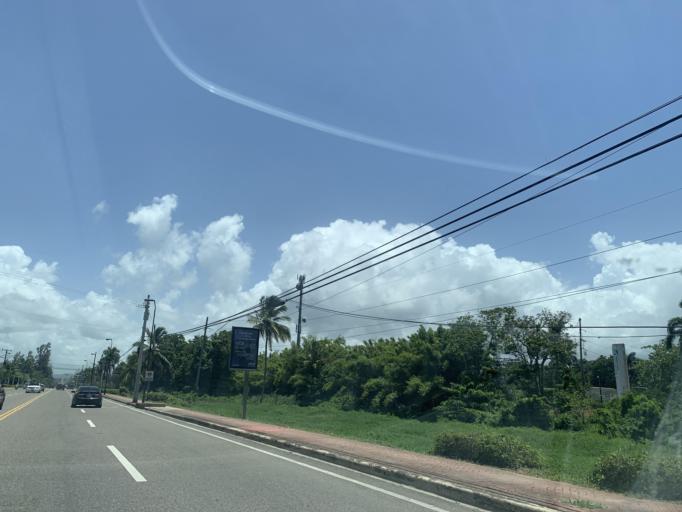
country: DO
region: Puerto Plata
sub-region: Puerto Plata
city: Puerto Plata
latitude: 19.7691
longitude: -70.6525
